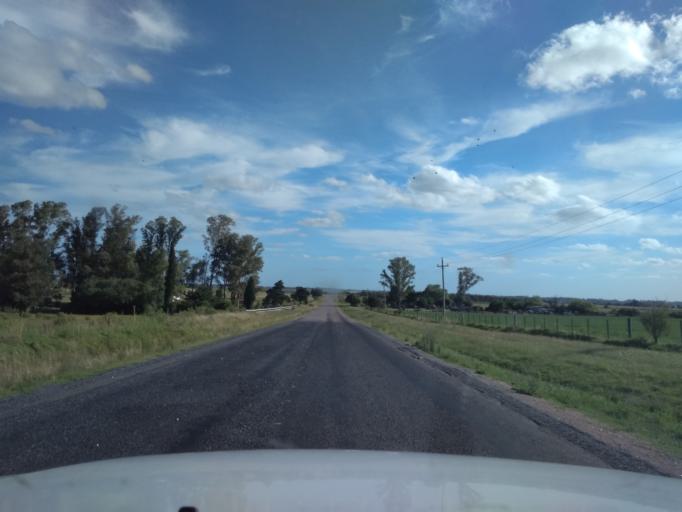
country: UY
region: Canelones
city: San Ramon
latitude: -34.2522
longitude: -55.9263
